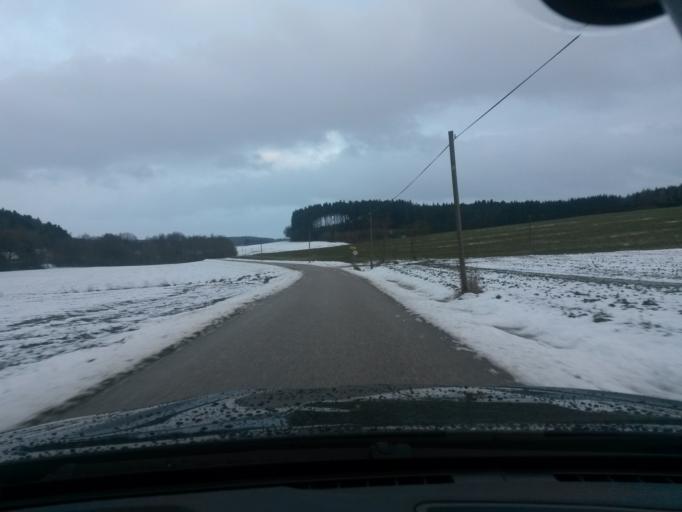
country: DE
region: Bavaria
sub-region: Lower Bavaria
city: Eching
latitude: 48.4871
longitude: 12.0649
